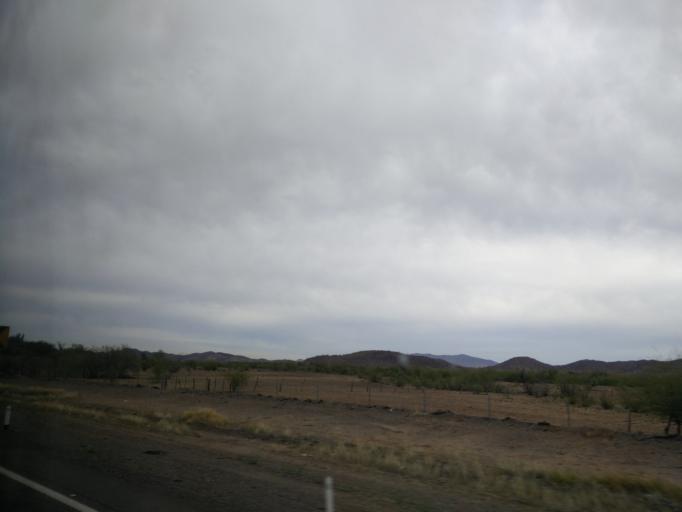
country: MX
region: Sonora
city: Hermosillo
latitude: 28.8996
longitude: -110.9510
